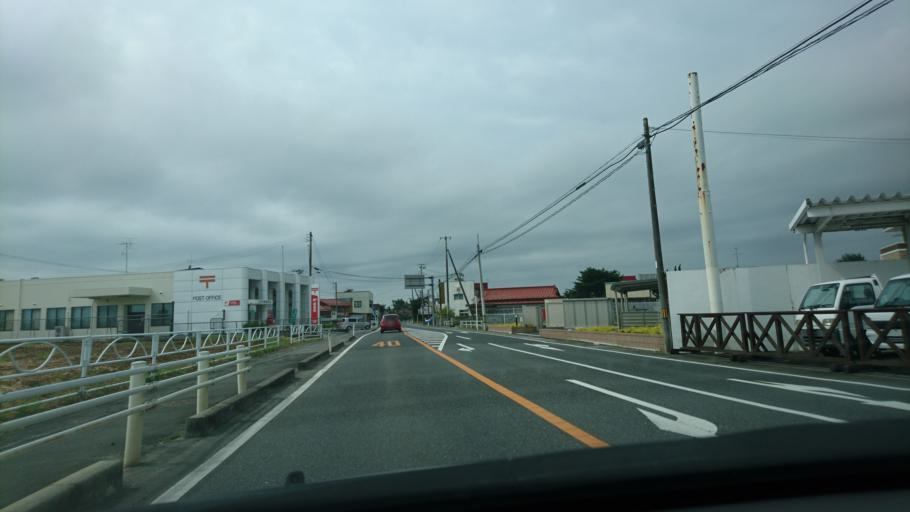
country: JP
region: Iwate
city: Ichinoseki
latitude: 38.7562
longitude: 141.0709
